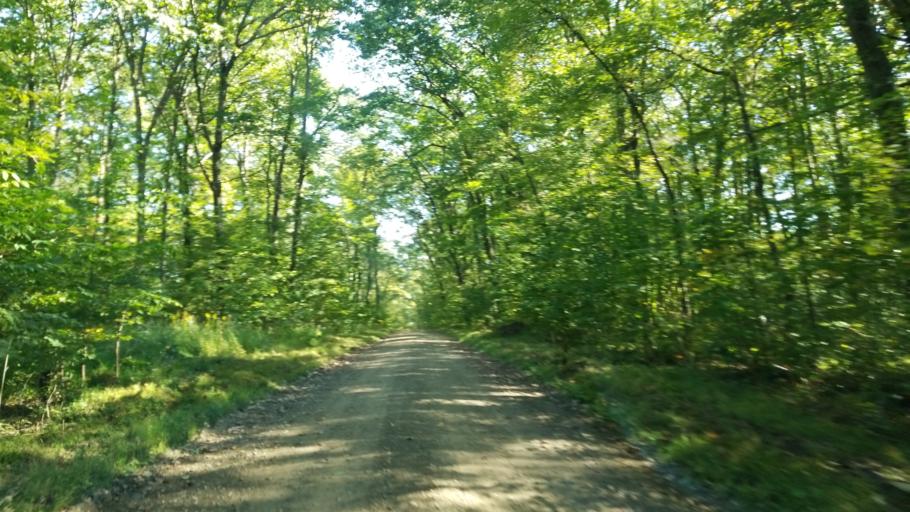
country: US
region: Pennsylvania
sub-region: Clearfield County
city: Curwensville
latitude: 41.1199
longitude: -78.5710
